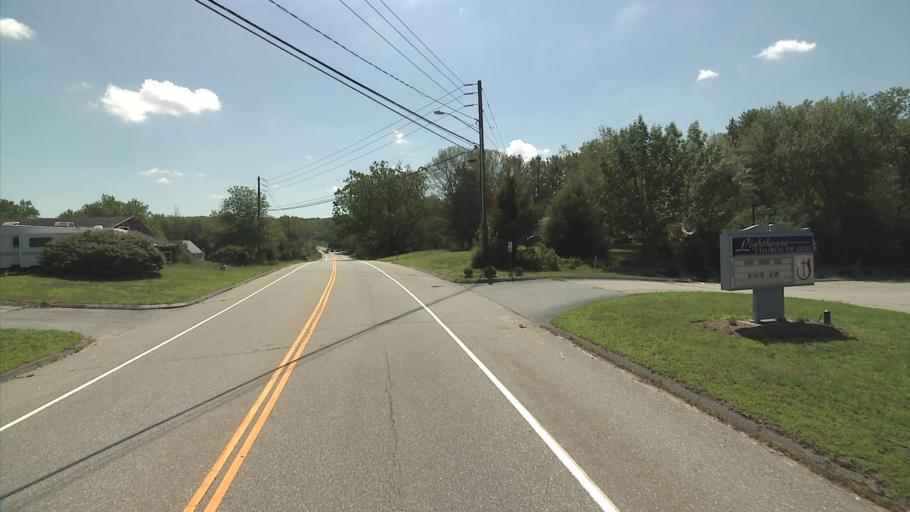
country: US
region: Connecticut
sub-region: Windham County
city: Plainfield
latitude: 41.6832
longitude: -71.9043
